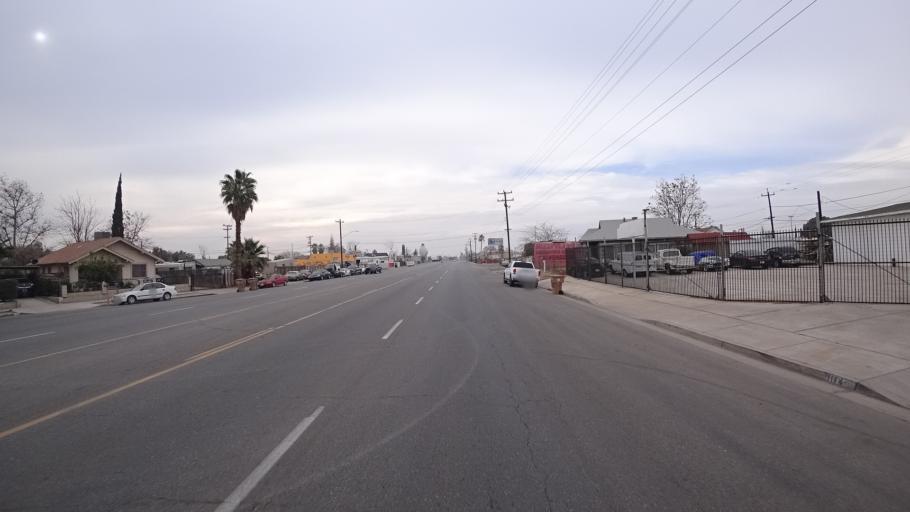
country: US
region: California
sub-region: Kern County
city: Bakersfield
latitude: 35.3733
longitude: -118.9866
